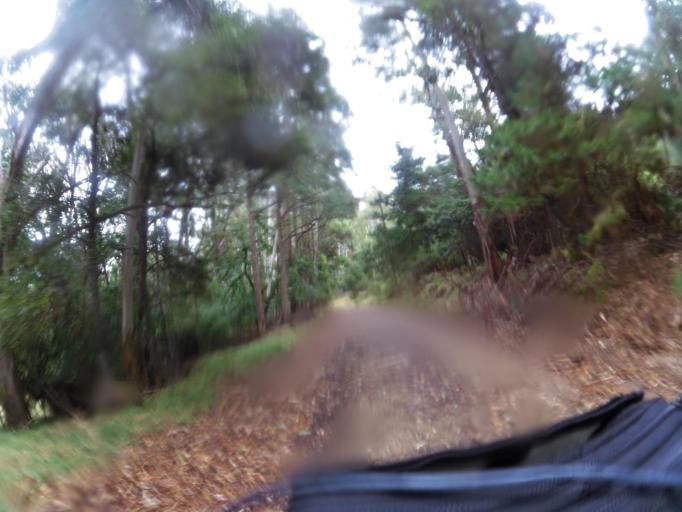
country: AU
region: New South Wales
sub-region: Greater Hume Shire
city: Holbrook
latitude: -36.1944
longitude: 147.5359
